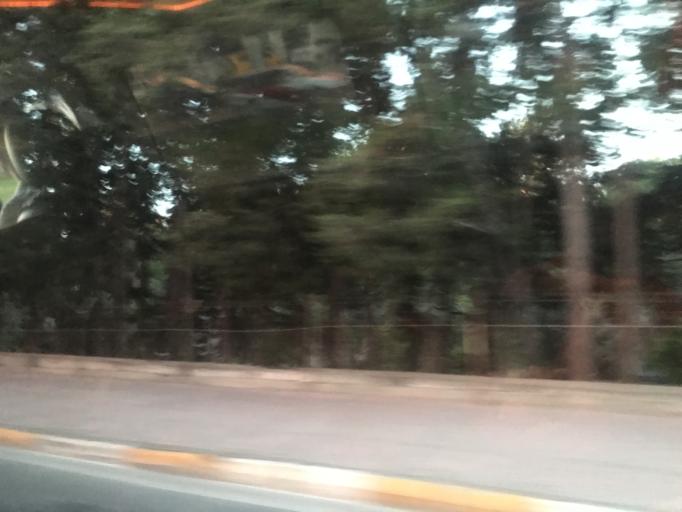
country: TR
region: Antalya
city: Antalya
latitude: 36.9155
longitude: 30.6751
